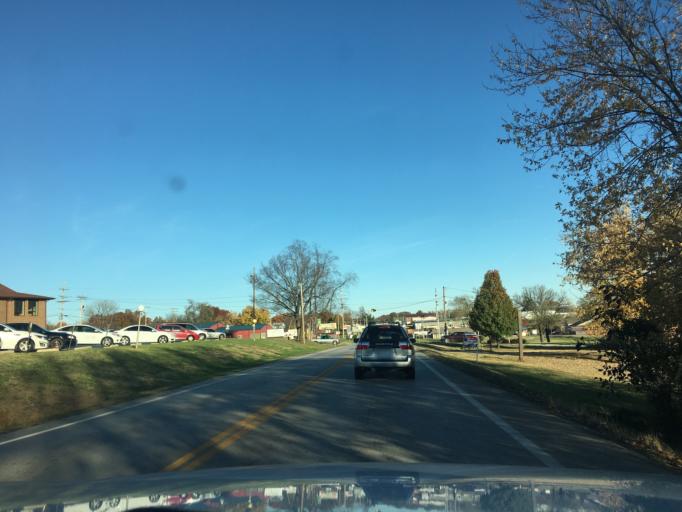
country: US
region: Missouri
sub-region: Franklin County
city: New Haven
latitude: 38.6006
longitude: -91.2266
